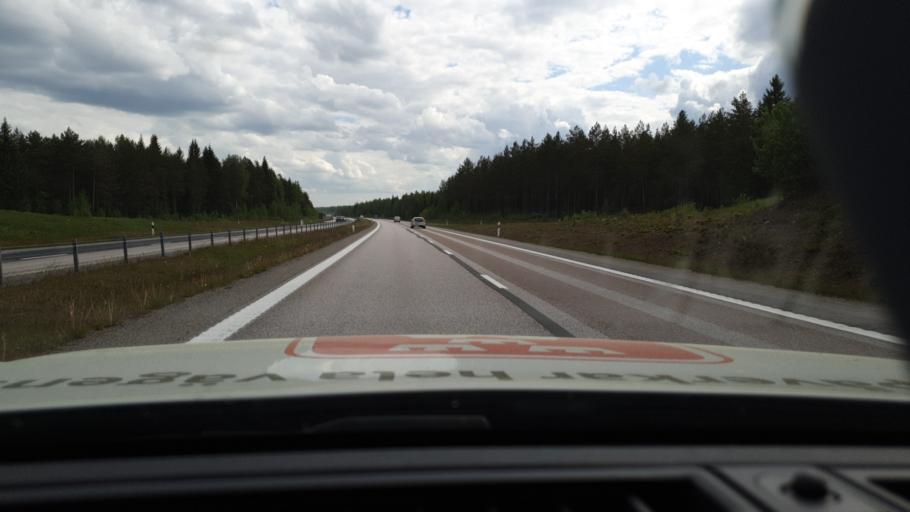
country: SE
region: Uppsala
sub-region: Tierps Kommun
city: Tierp
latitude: 60.2144
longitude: 17.4957
